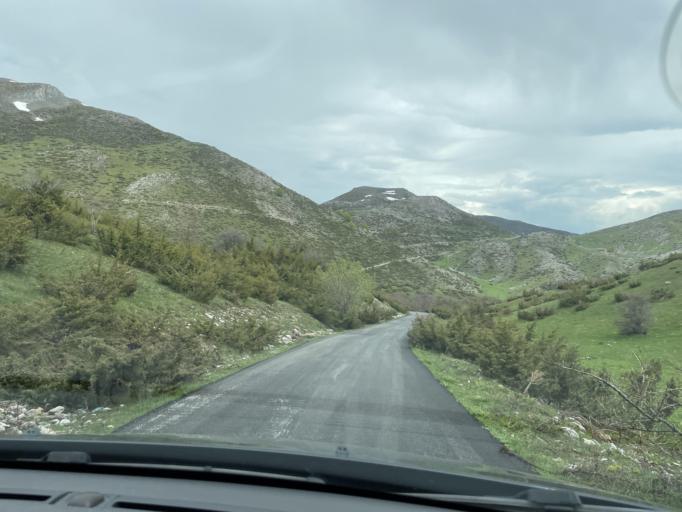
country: MK
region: Opstina Rostusa
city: Rostusha
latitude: 41.6253
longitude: 20.6812
